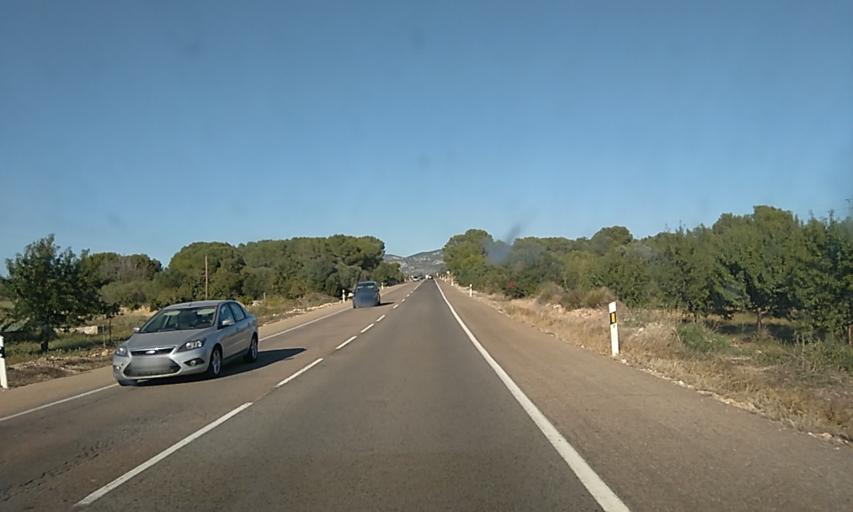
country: ES
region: Valencia
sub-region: Provincia de Castello
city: Torreblanca
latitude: 40.2408
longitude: 0.2276
